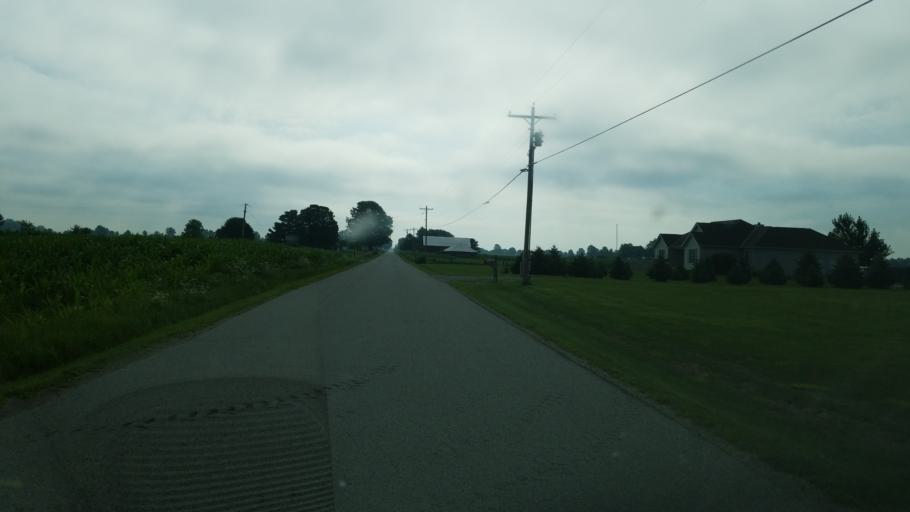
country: US
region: Ohio
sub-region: Morrow County
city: Cardington
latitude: 40.5576
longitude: -82.9399
